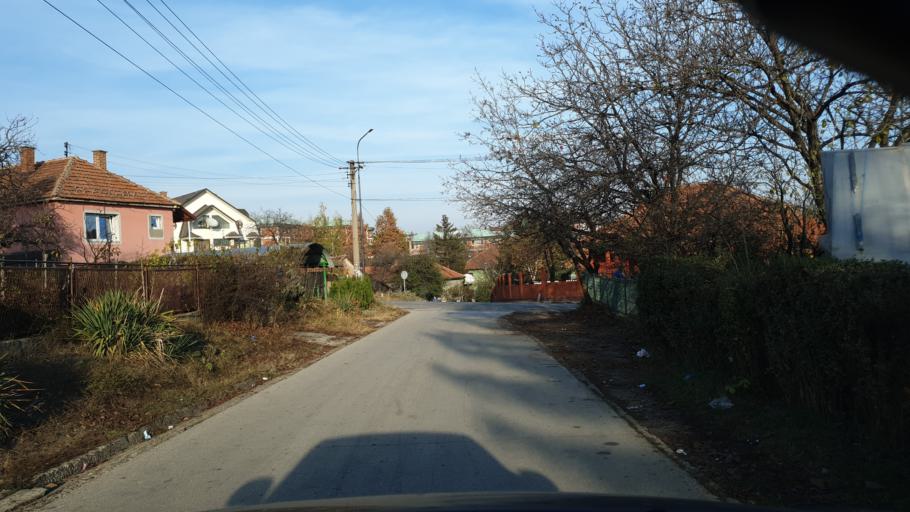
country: RS
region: Central Serbia
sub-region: Borski Okrug
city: Bor
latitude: 44.0536
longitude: 22.1004
